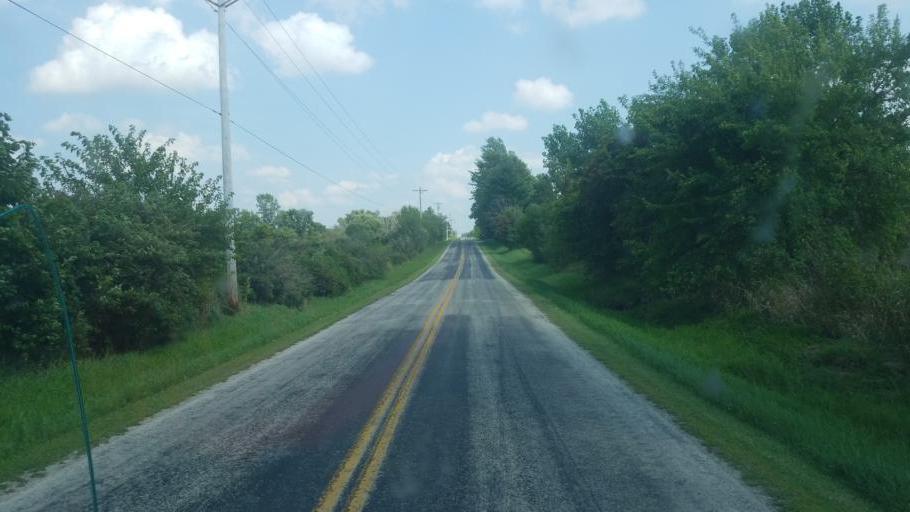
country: US
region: Ohio
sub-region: Huron County
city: New London
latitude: 41.0577
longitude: -82.2795
